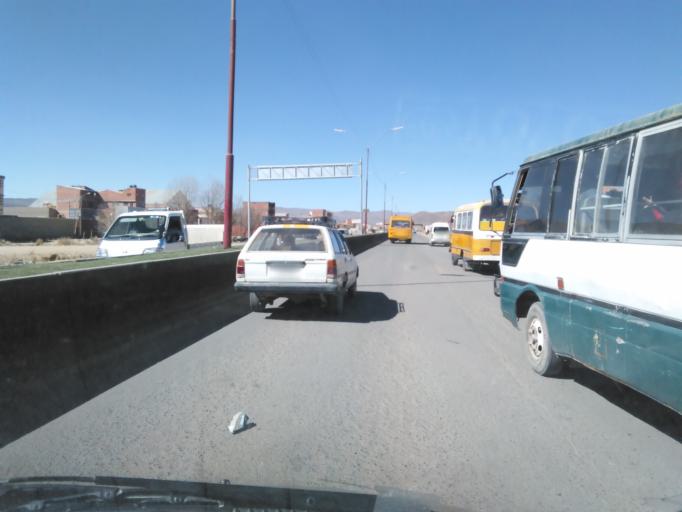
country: BO
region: Oruro
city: Oruro
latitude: -17.9733
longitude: -67.0845
